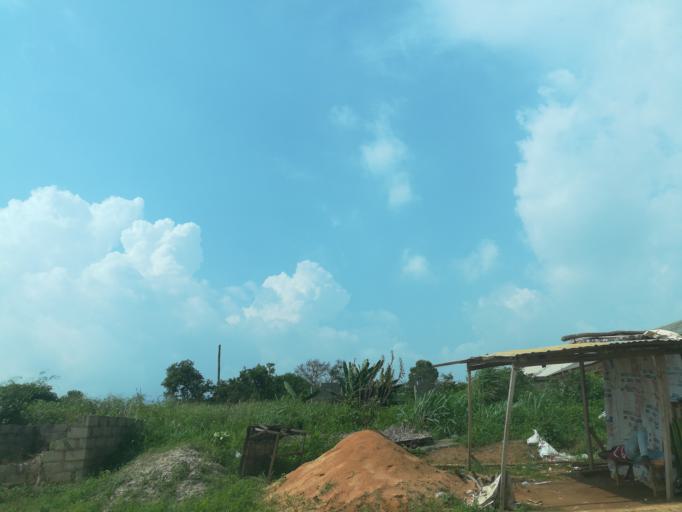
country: NG
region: Lagos
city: Ikorodu
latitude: 6.6403
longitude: 3.6683
